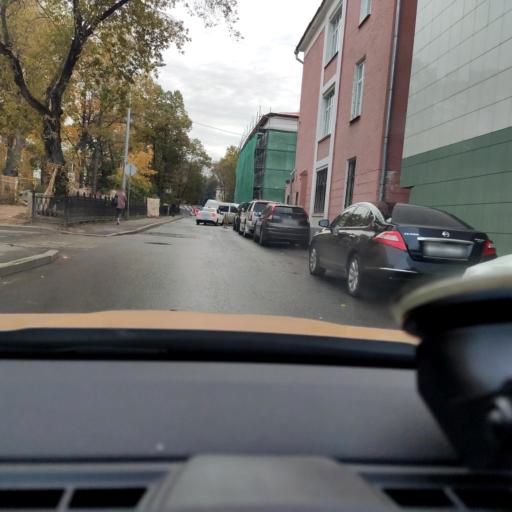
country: RU
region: Moskovskaya
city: Presnenskiy
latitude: 55.7796
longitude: 37.5529
